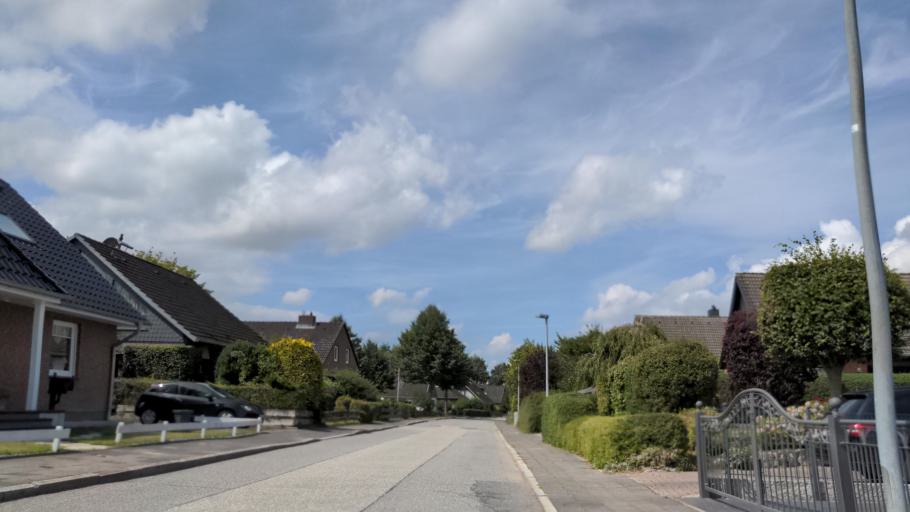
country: DE
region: Schleswig-Holstein
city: Eutin
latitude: 54.1222
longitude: 10.6105
